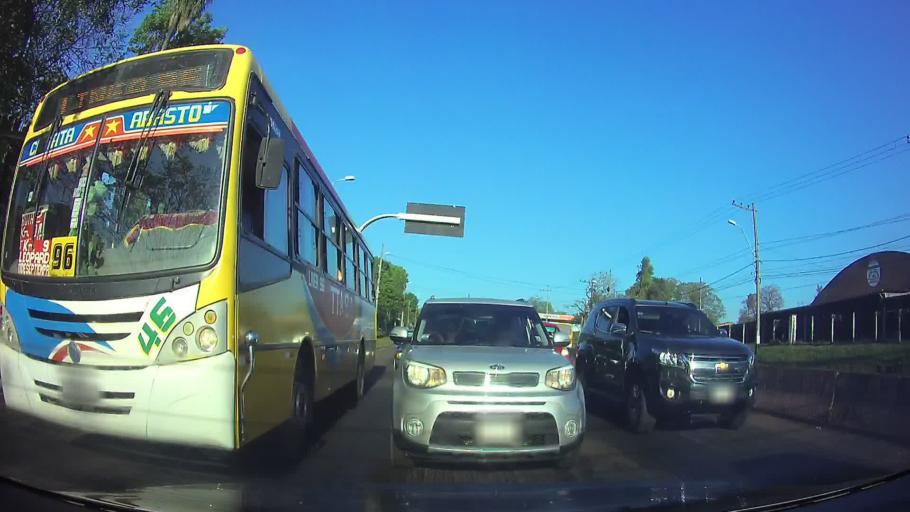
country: PY
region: Central
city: Capiata
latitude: -25.3487
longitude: -57.4605
